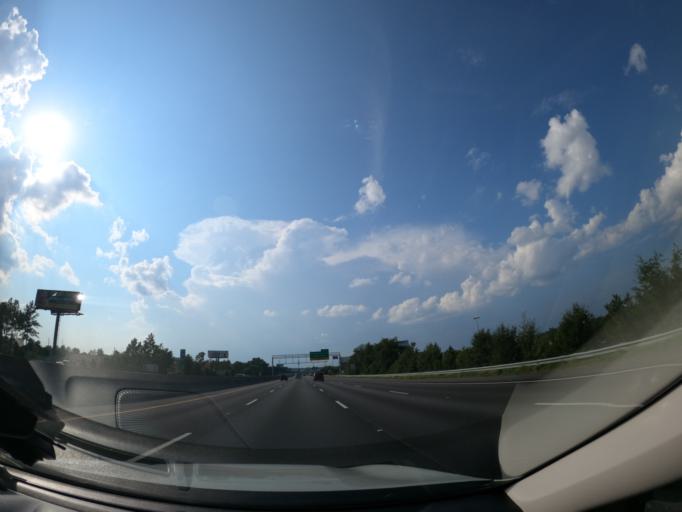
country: US
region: Georgia
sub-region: Columbia County
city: Martinez
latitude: 33.4580
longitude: -82.0772
